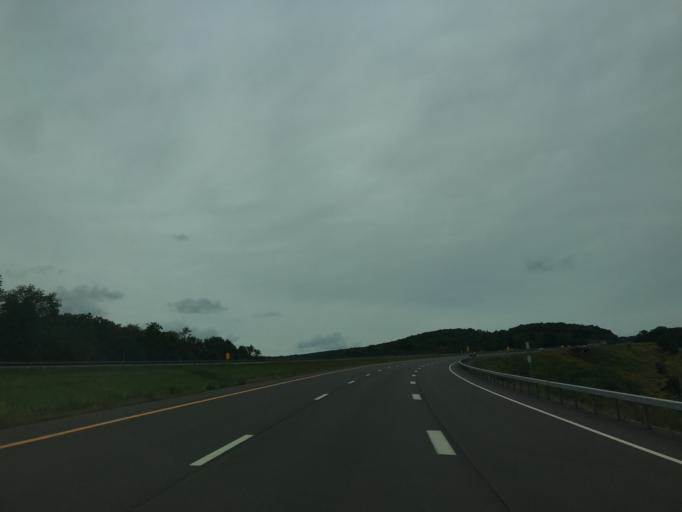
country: US
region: New York
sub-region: Broome County
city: Chenango Bridge
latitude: 42.1778
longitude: -75.7500
